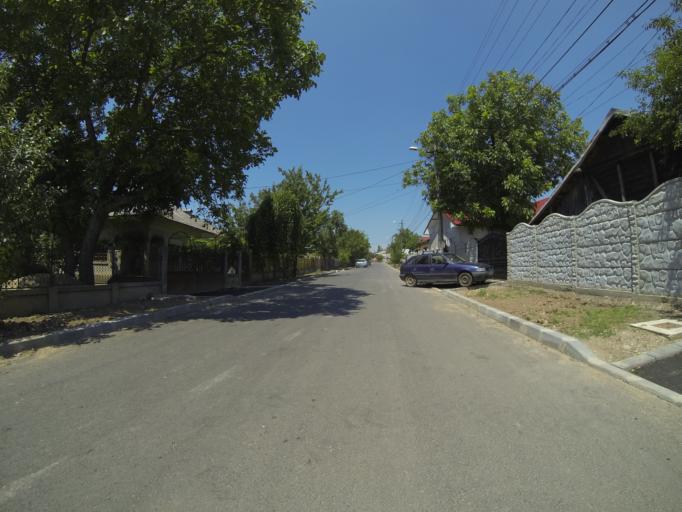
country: RO
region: Dolj
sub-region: Comuna Segarcea
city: Segarcea
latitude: 44.0911
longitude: 23.7417
